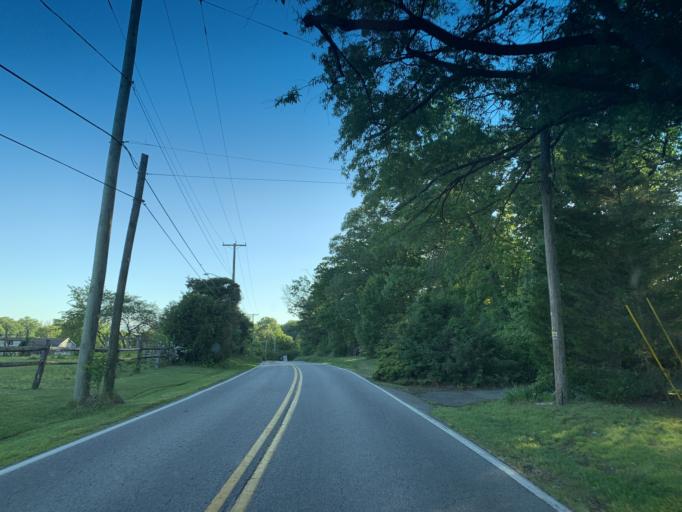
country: US
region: Maryland
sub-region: Cecil County
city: Elkton
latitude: 39.6653
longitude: -75.8444
